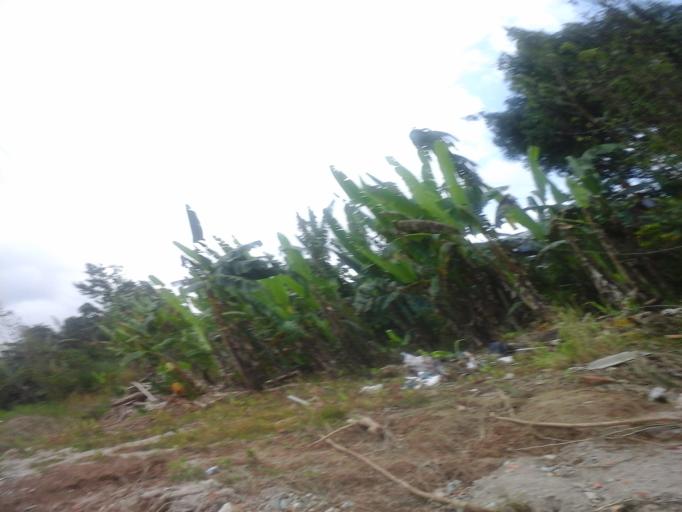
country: CO
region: Putumayo
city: Mocoa
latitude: 1.1722
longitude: -76.6627
